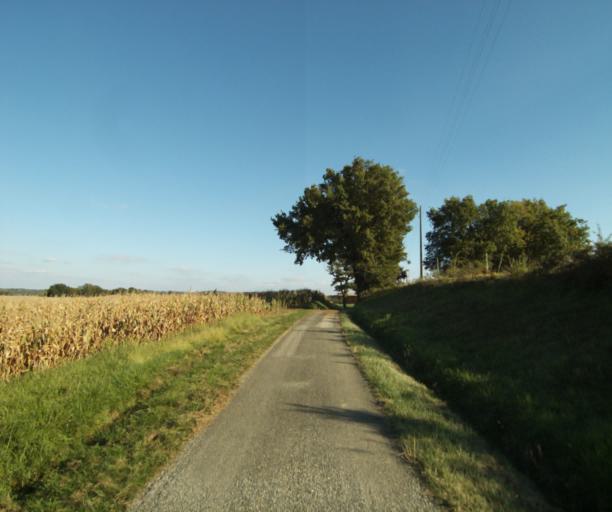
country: FR
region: Midi-Pyrenees
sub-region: Departement du Gers
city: Eauze
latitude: 43.7835
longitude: 0.1348
